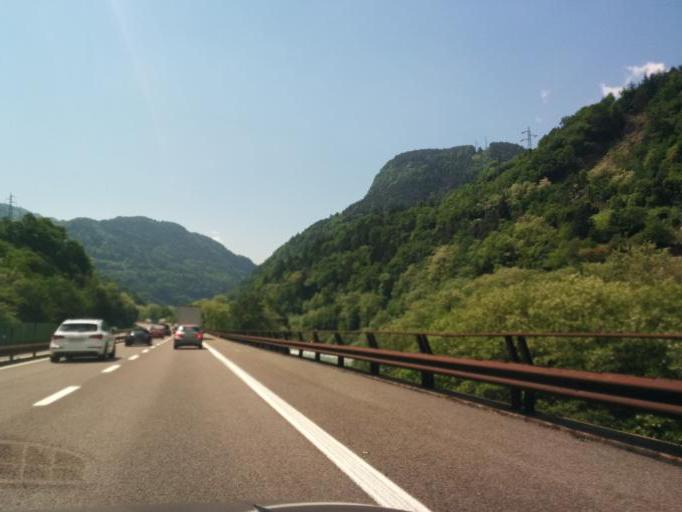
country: IT
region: Trentino-Alto Adige
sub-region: Bolzano
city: Ponte Gardena
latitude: 46.5801
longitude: 11.5237
